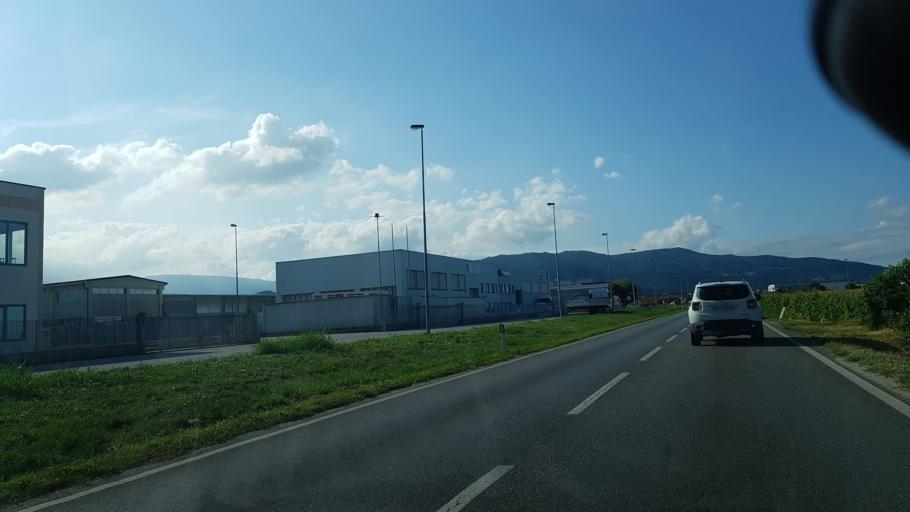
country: IT
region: Piedmont
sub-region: Provincia di Cuneo
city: Busca
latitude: 44.4954
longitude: 7.4950
